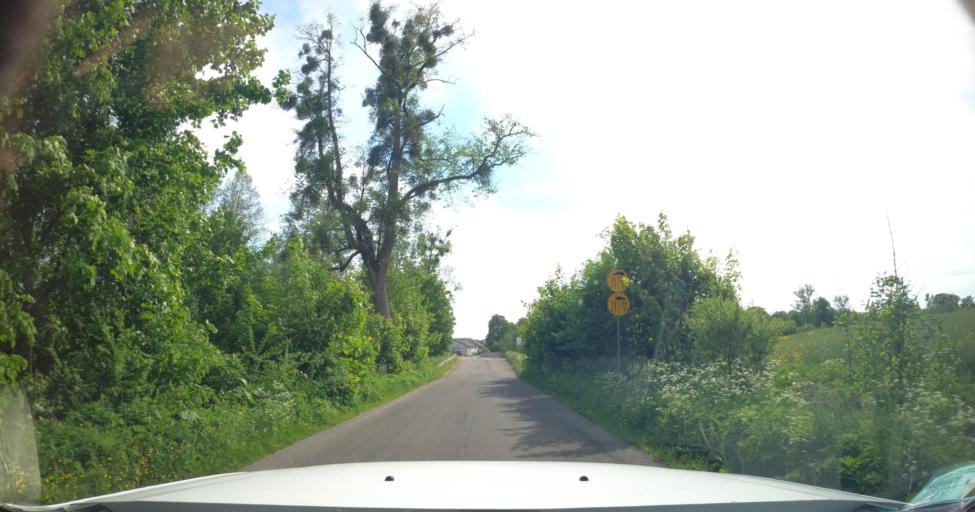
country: PL
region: Warmian-Masurian Voivodeship
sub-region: Powiat ostrodzki
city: Milakowo
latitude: 54.0112
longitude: 20.1470
